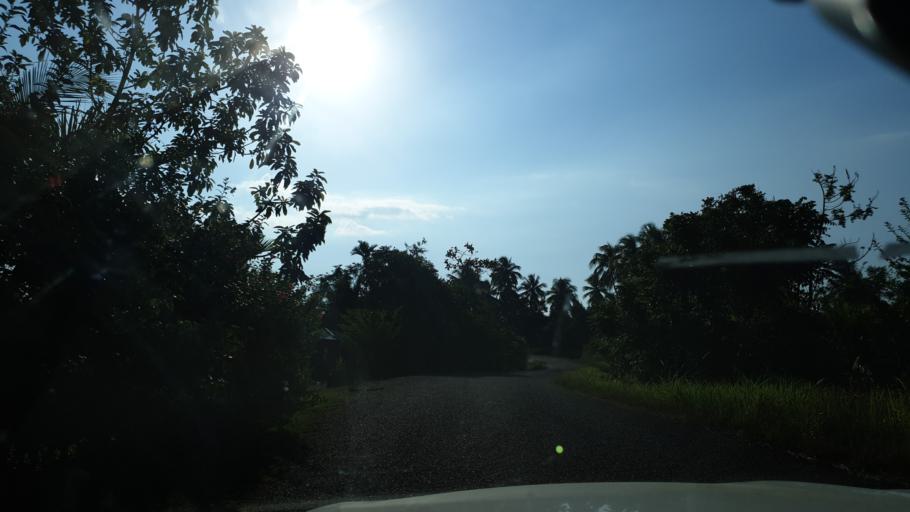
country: PG
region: East Sepik
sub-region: Wewak
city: Wewak
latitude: -3.6964
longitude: 143.6478
